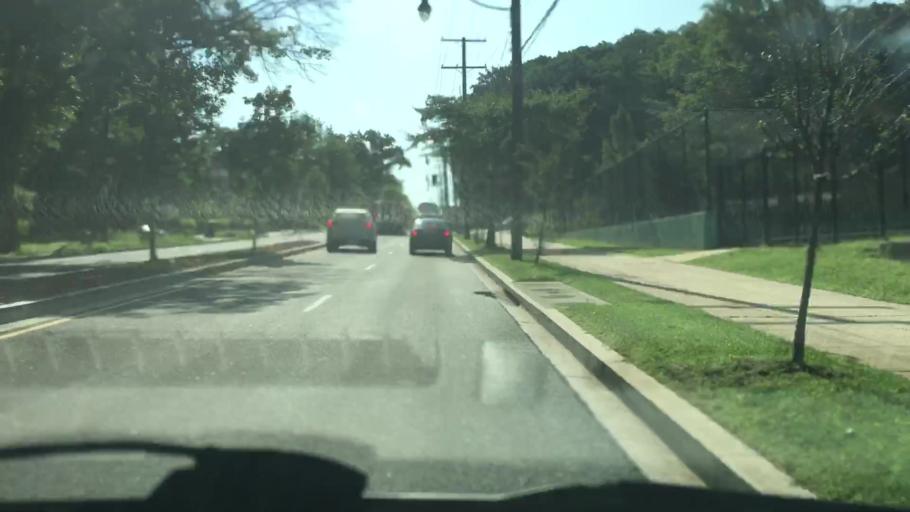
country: US
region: Maryland
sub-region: Prince George's County
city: Silver Hill
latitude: 38.8707
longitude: -76.9641
